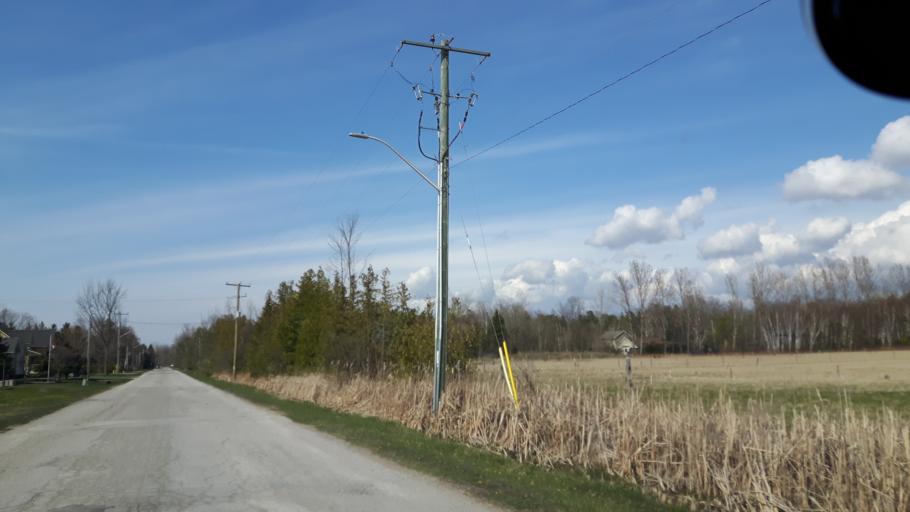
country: CA
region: Ontario
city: Bluewater
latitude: 43.5523
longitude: -81.7006
